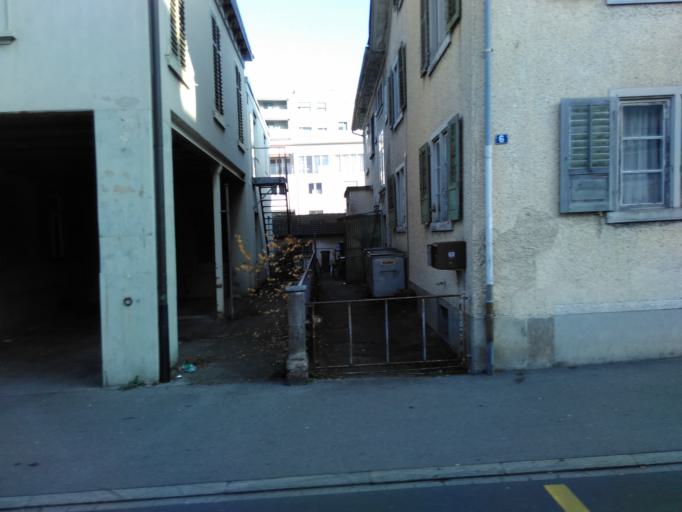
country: CH
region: Schwyz
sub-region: Bezirk March
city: Schubelbach
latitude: 47.1753
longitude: 8.8983
